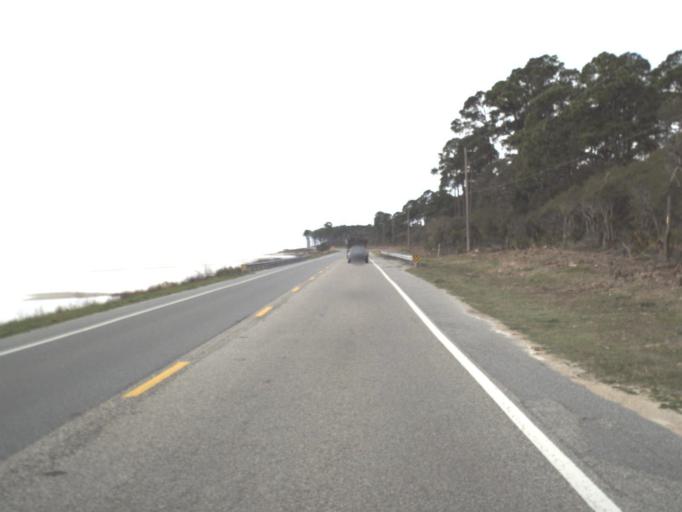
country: US
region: Florida
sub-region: Franklin County
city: Eastpoint
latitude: 29.7758
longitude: -84.7882
